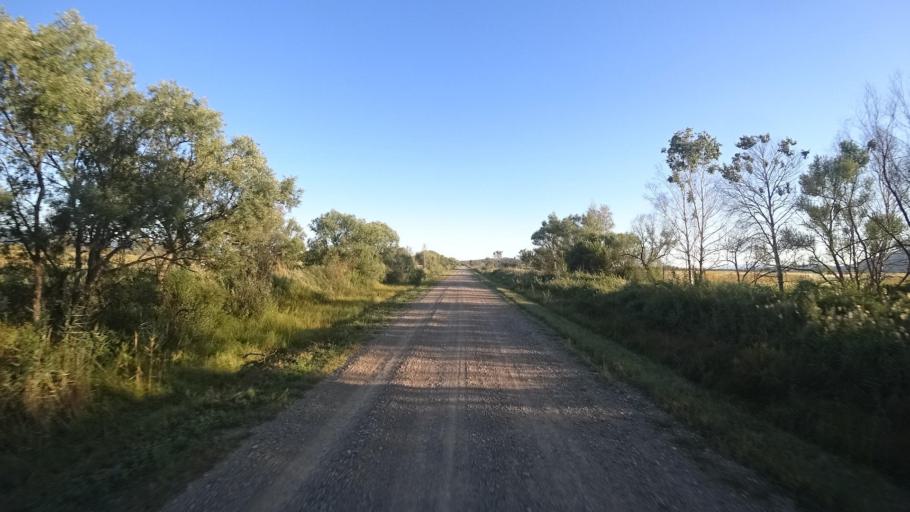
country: RU
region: Primorskiy
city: Kirovskiy
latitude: 44.7986
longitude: 133.6213
